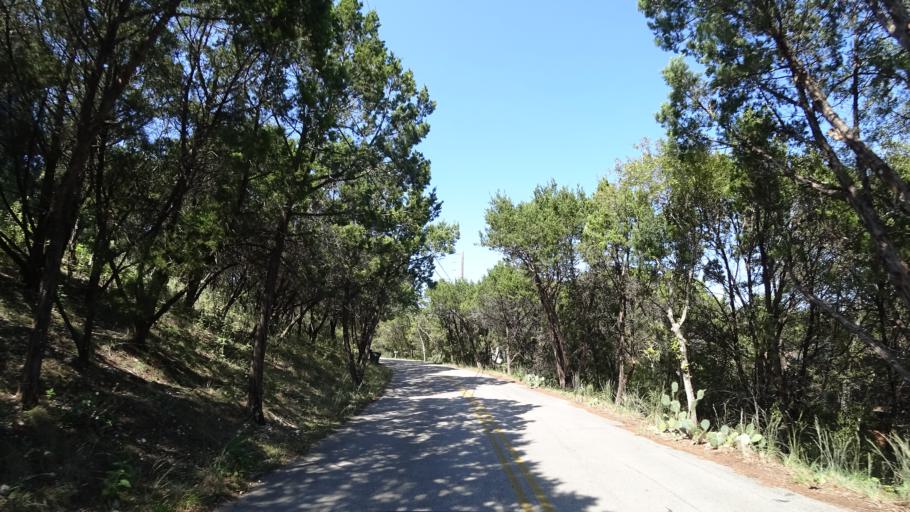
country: US
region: Texas
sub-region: Travis County
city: West Lake Hills
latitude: 30.3048
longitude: -97.7985
